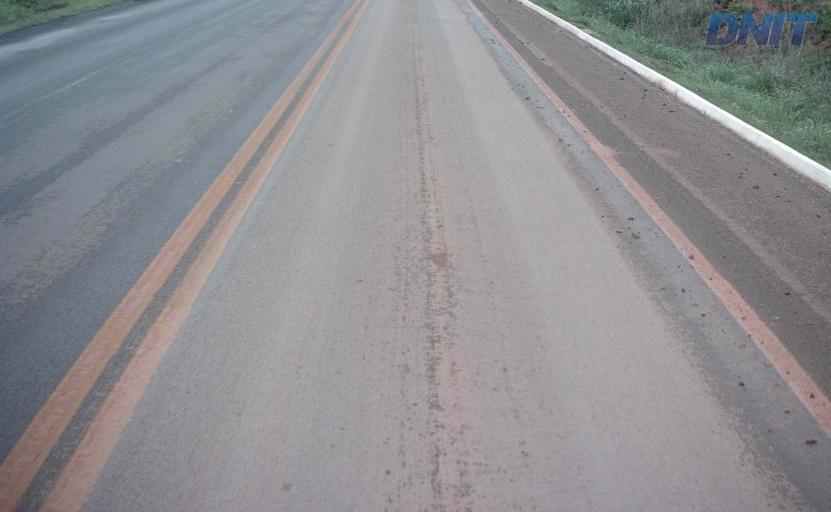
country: BR
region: Goias
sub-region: Padre Bernardo
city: Padre Bernardo
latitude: -15.1516
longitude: -48.3357
